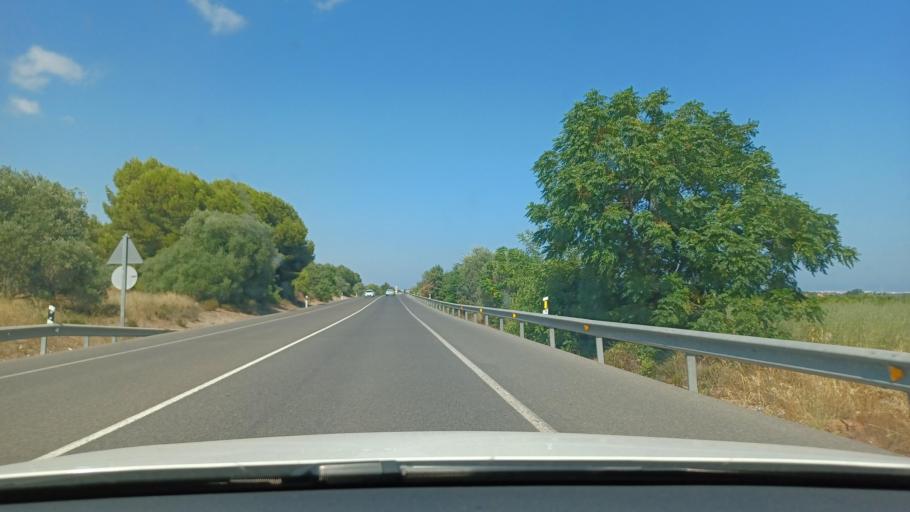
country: ES
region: Valencia
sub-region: Provincia de Castello
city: Chilches
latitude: 39.7728
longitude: -0.2050
